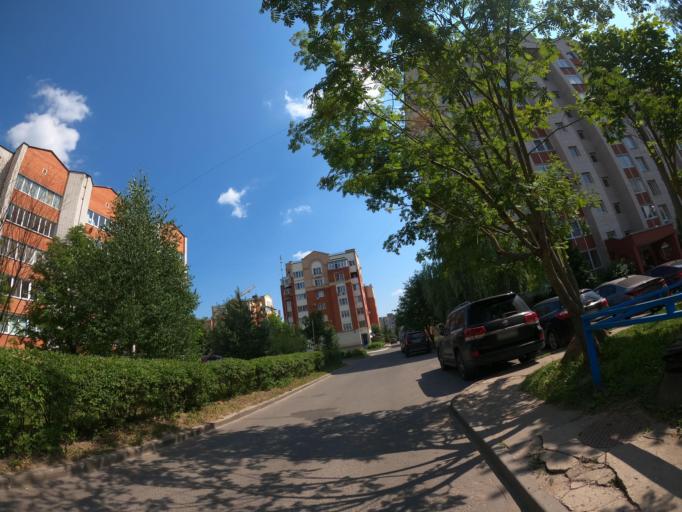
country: RU
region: Kaluga
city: Obninsk
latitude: 55.1156
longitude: 36.5860
